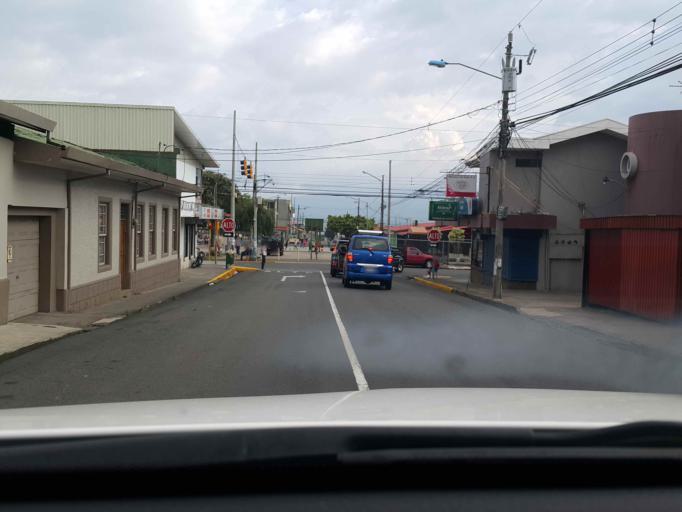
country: CR
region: Heredia
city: San Josecito
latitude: 10.0158
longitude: -84.1001
